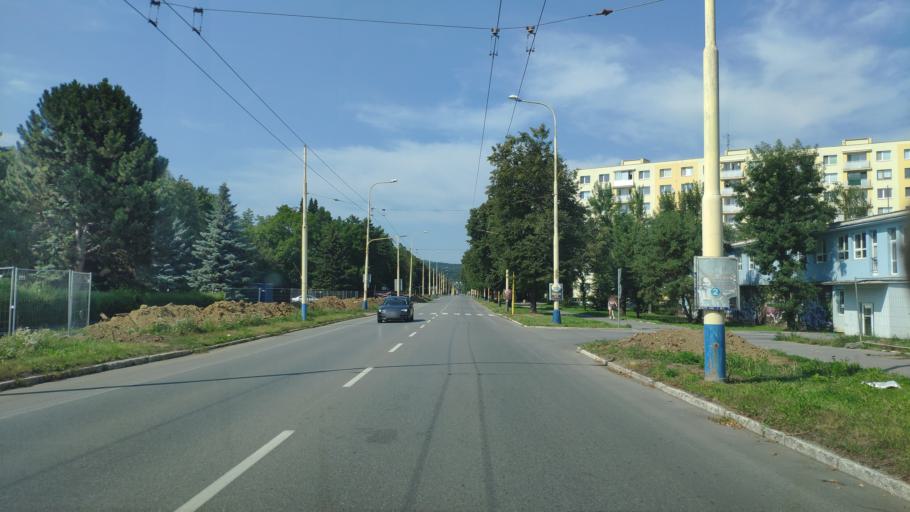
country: SK
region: Presovsky
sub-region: Okres Presov
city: Presov
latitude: 49.0045
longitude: 21.2210
